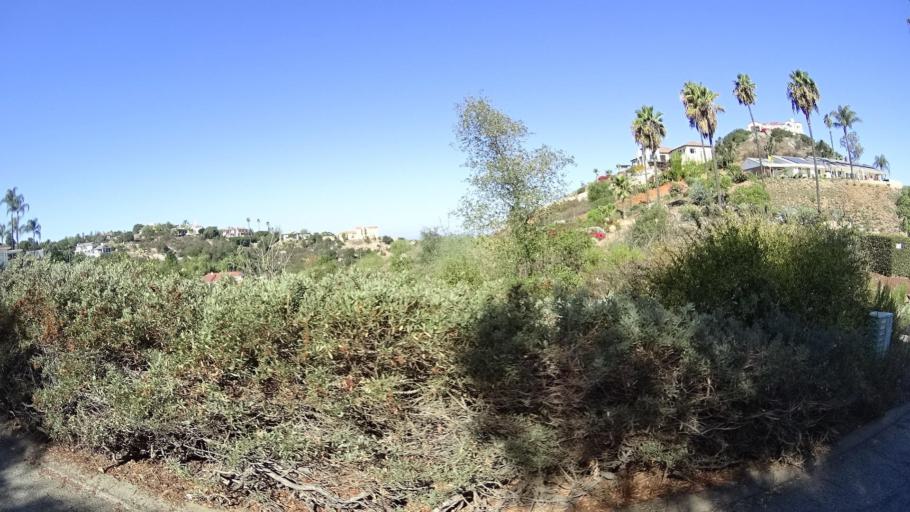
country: US
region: California
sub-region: San Diego County
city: Hidden Meadows
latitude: 33.2304
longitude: -117.1208
